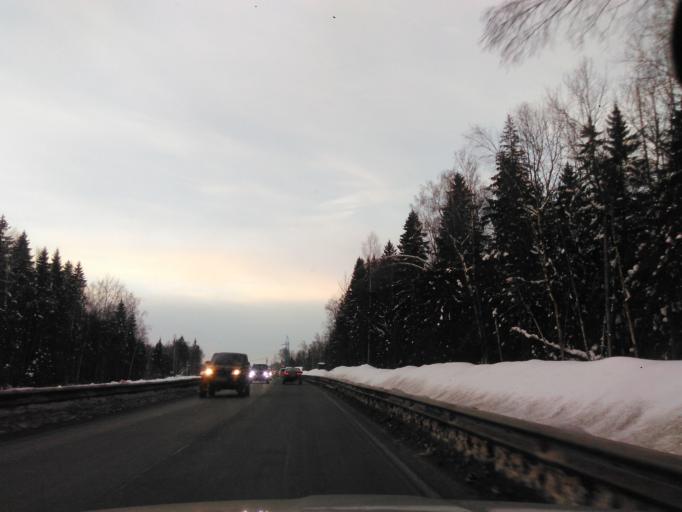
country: RU
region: Moskovskaya
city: Povarovo
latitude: 56.0146
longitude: 37.0286
